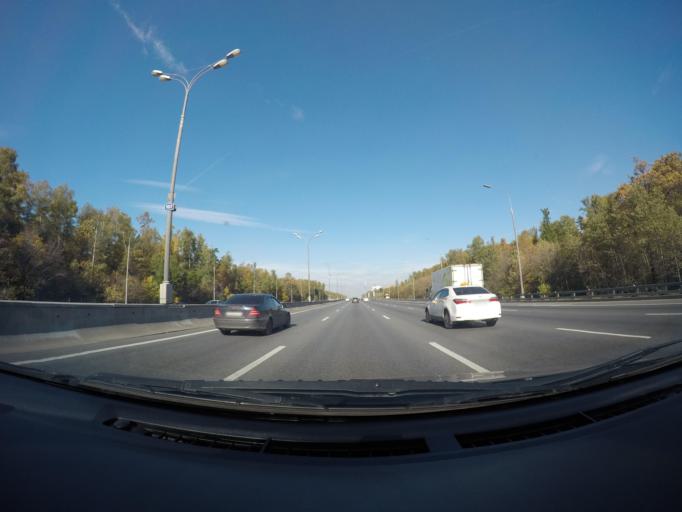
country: RU
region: Moscow
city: Ivanovskoye
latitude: 55.7899
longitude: 37.8414
